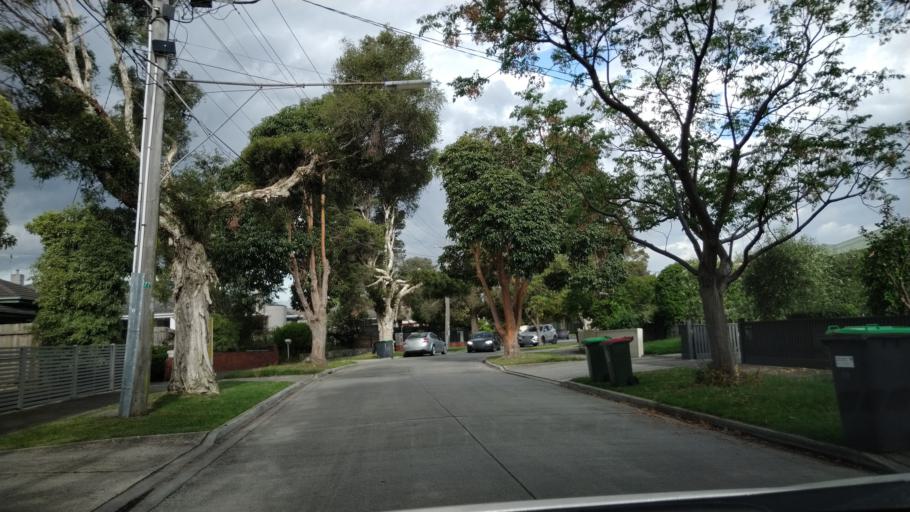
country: AU
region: Victoria
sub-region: Glen Eira
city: Carnegie
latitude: -37.8972
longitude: 145.0538
